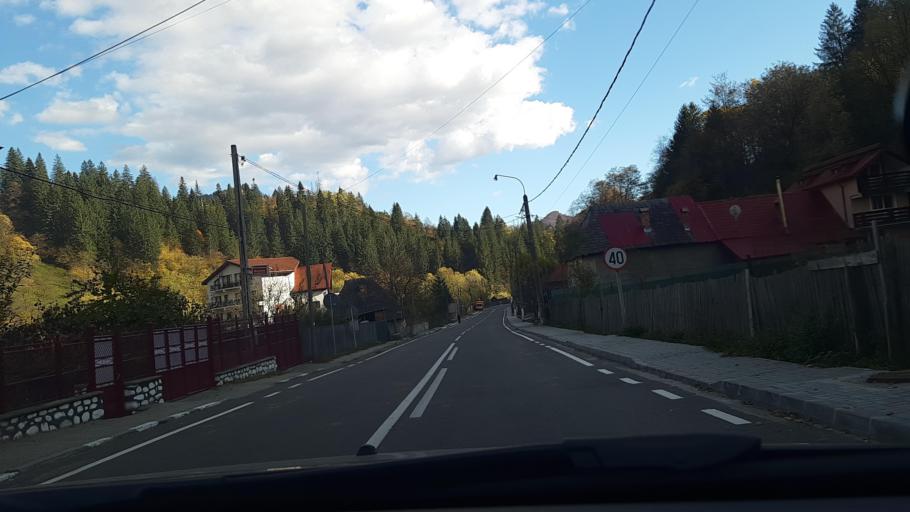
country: RO
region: Valcea
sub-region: Comuna Voineasa
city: Voineasa
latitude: 45.4254
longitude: 23.9495
